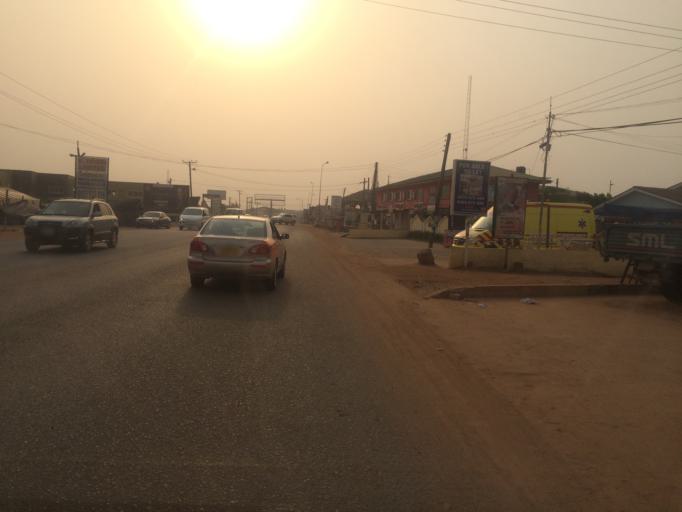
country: GH
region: Greater Accra
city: Nungua
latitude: 5.6341
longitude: -0.0985
